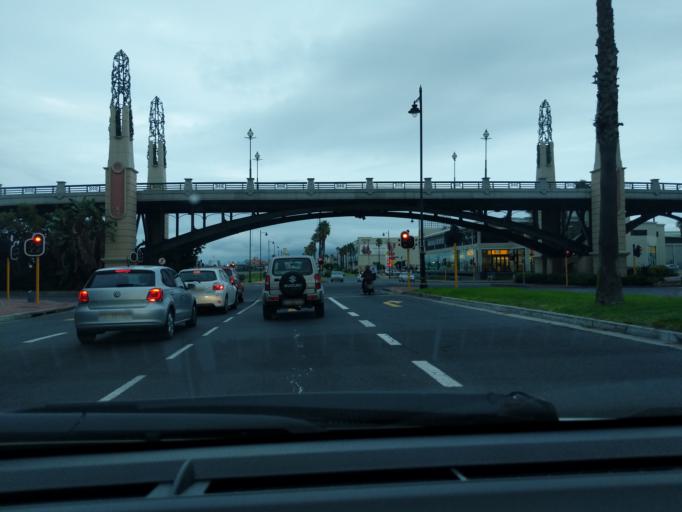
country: ZA
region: Western Cape
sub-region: City of Cape Town
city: Sunset Beach
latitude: -33.8916
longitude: 18.5164
